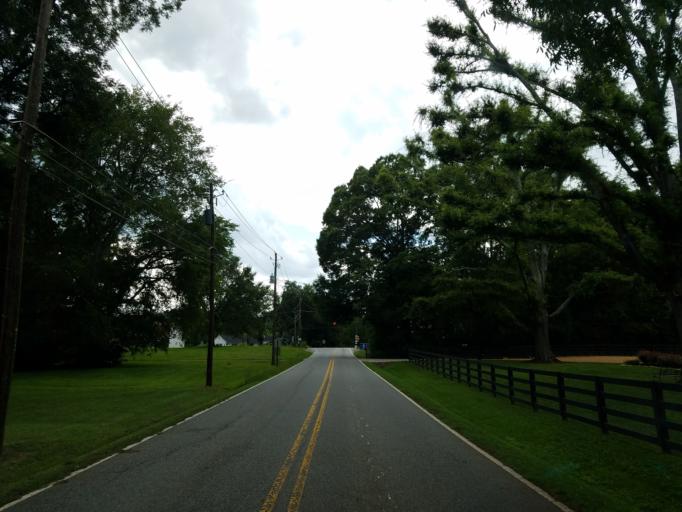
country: US
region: Georgia
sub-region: Bartow County
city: Cartersville
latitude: 34.2494
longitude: -84.8511
